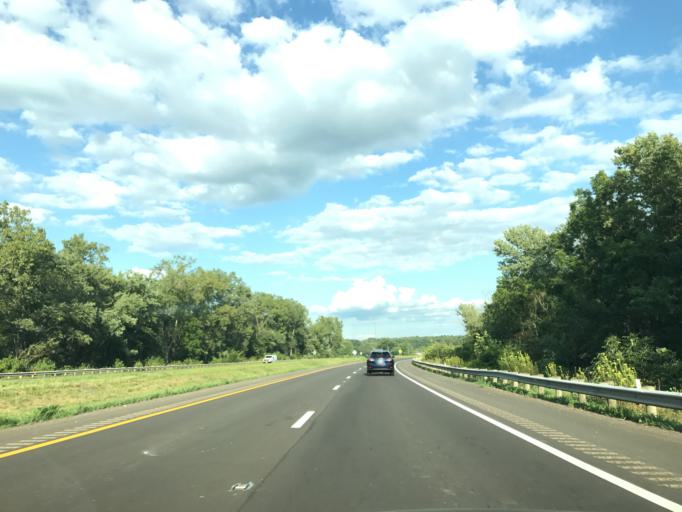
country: US
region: Ohio
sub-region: Ashland County
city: Loudonville
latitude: 40.7852
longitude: -82.1646
